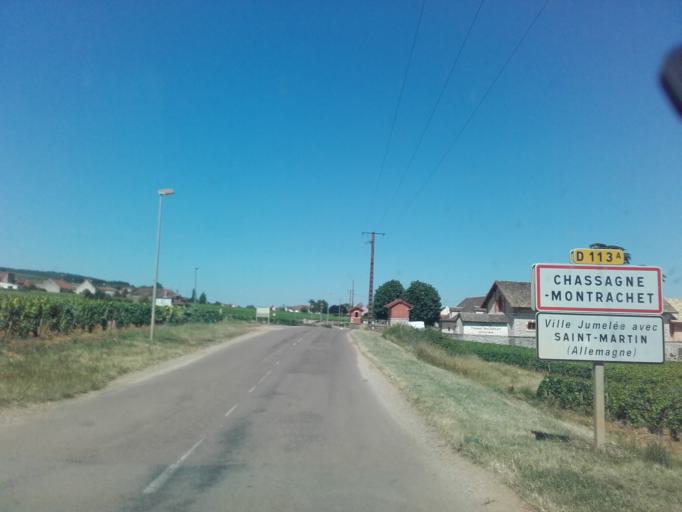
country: FR
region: Bourgogne
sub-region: Departement de la Cote-d'Or
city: Corpeau
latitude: 46.9330
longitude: 4.7273
